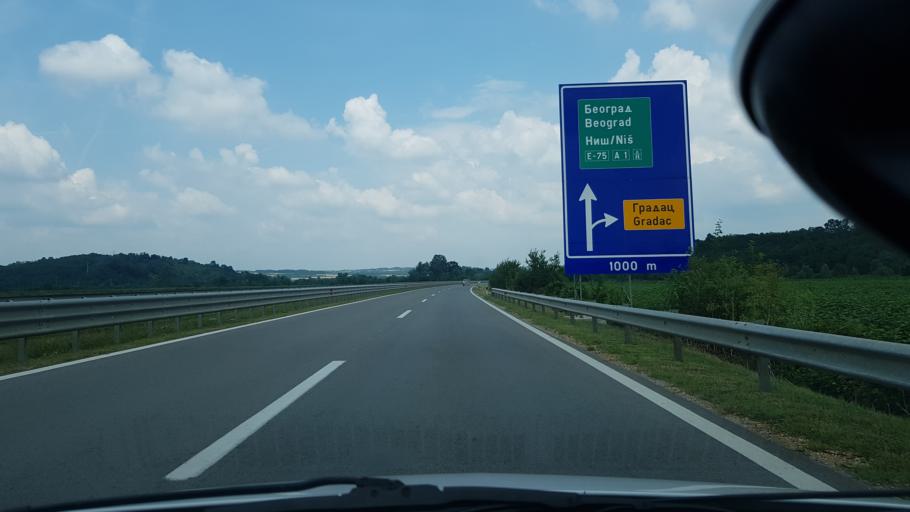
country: RS
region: Central Serbia
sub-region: Sumadijski Okrug
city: Batocina
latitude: 44.1329
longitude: 21.0202
